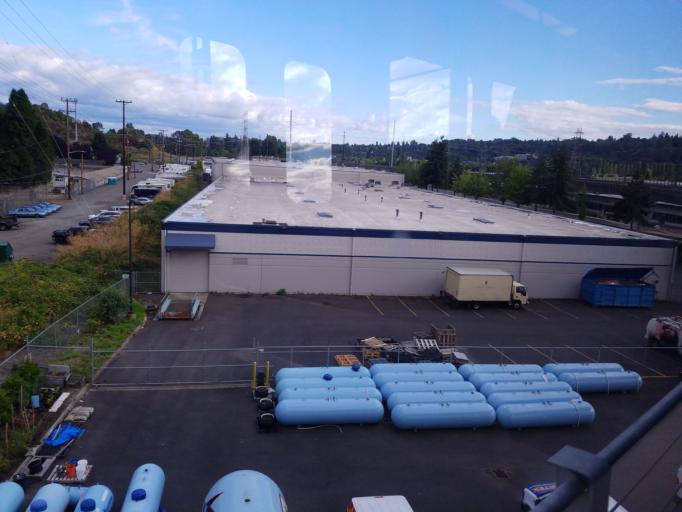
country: US
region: Washington
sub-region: King County
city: Riverton
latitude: 47.5064
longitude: -122.2897
